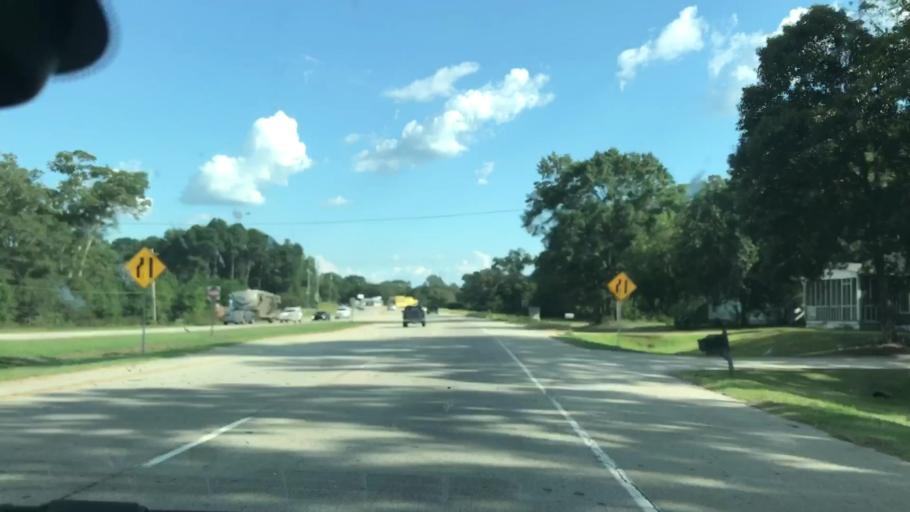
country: US
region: Georgia
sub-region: Troup County
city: La Grange
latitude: 32.9968
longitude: -85.0099
